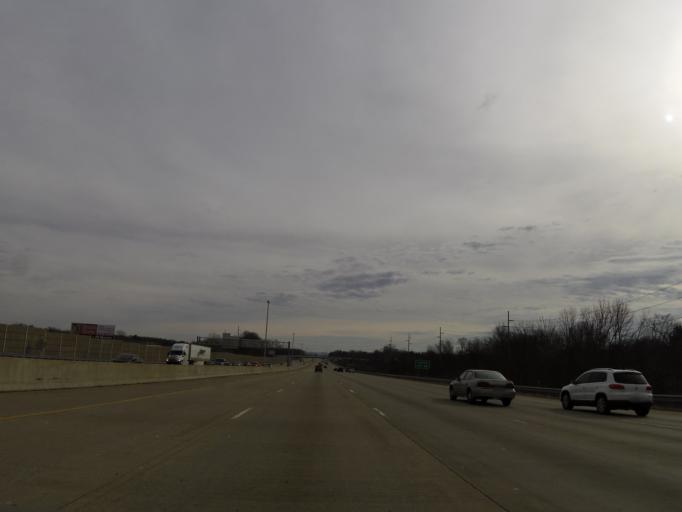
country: US
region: Indiana
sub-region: Marion County
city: Meridian Hills
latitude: 39.9276
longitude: -86.1342
